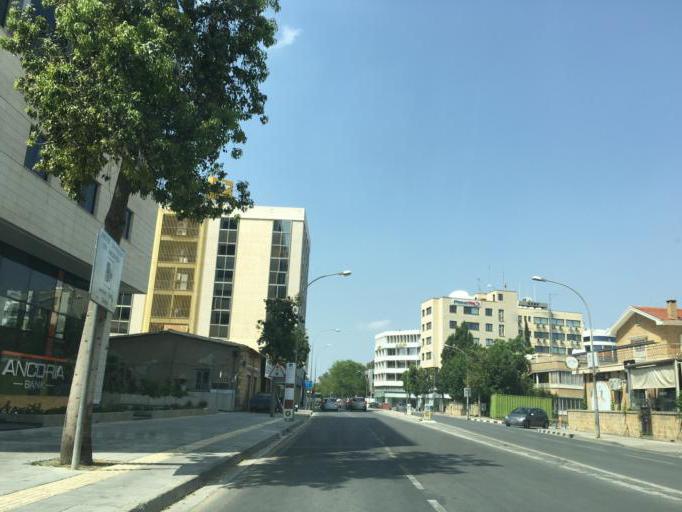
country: CY
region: Lefkosia
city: Nicosia
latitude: 35.1623
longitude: 33.3537
